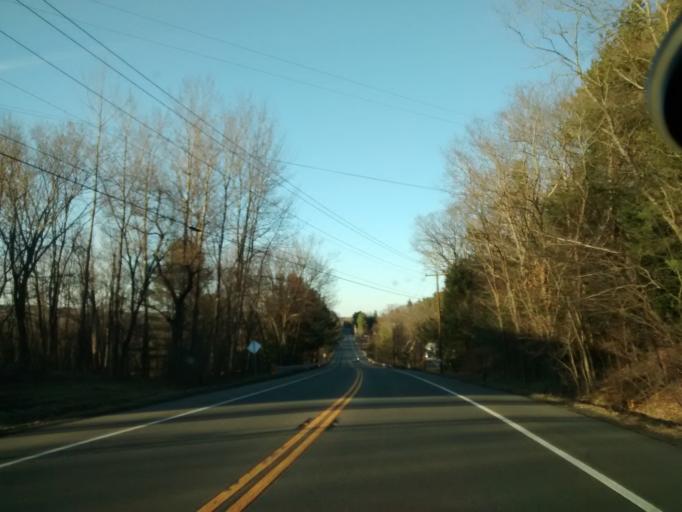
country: US
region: Massachusetts
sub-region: Worcester County
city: Warren
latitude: 42.2230
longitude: -72.1712
